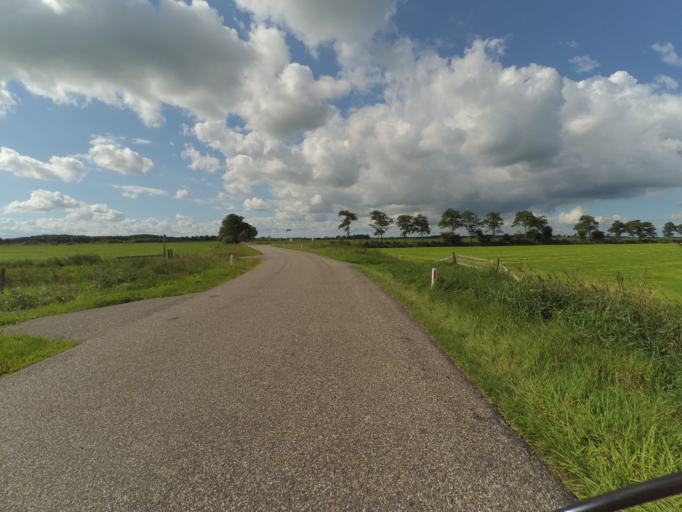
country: NL
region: Friesland
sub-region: Gemeente Tytsjerksteradiel
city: Hurdegaryp
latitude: 53.2430
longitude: 5.9403
